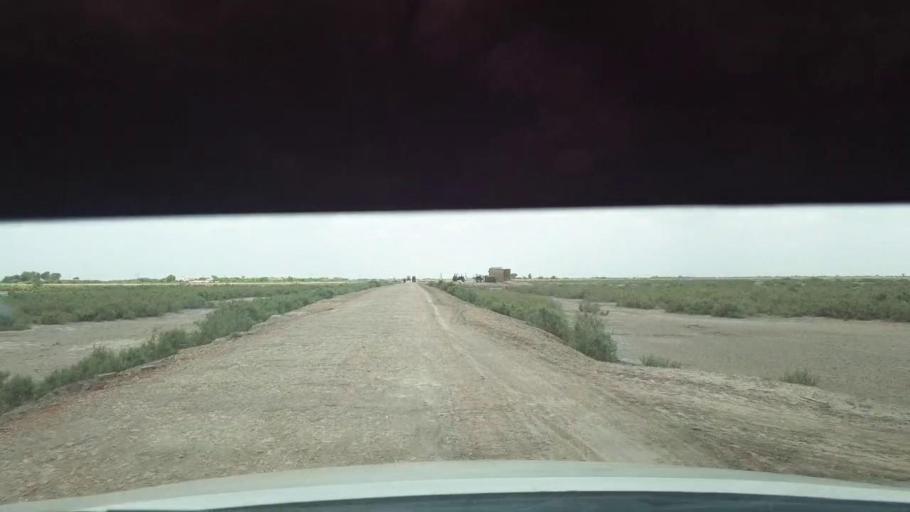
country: PK
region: Sindh
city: Kadhan
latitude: 24.5470
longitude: 69.1249
